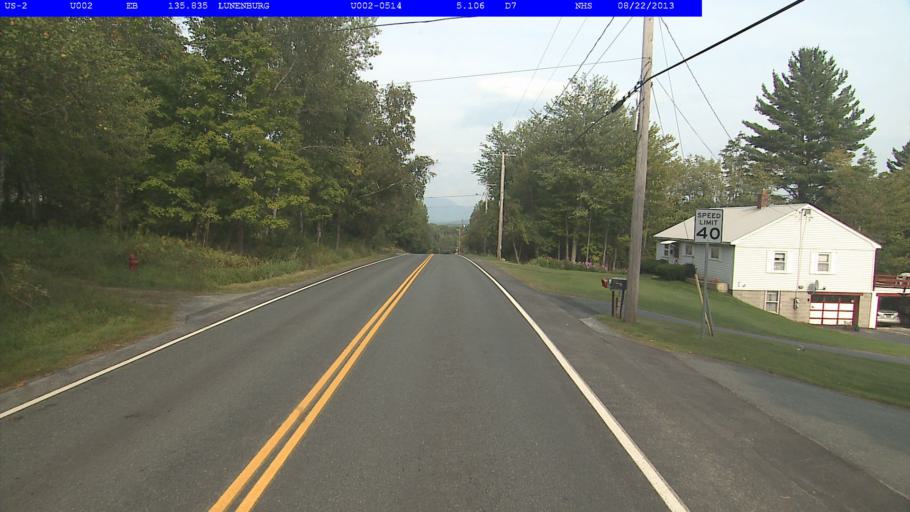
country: US
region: New Hampshire
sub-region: Coos County
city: Lancaster
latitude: 44.4636
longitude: -71.6740
